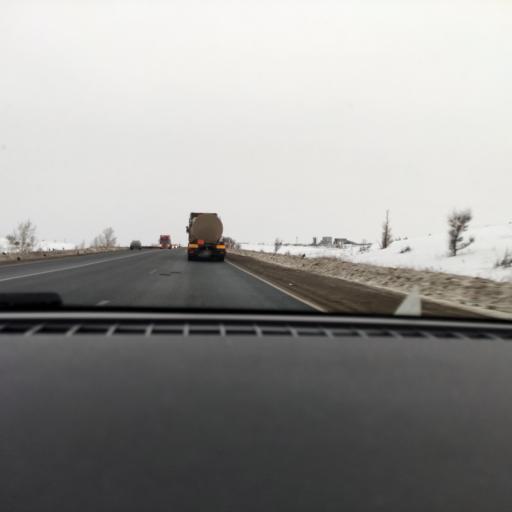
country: RU
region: Samara
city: Novosemeykino
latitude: 53.3833
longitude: 50.4297
